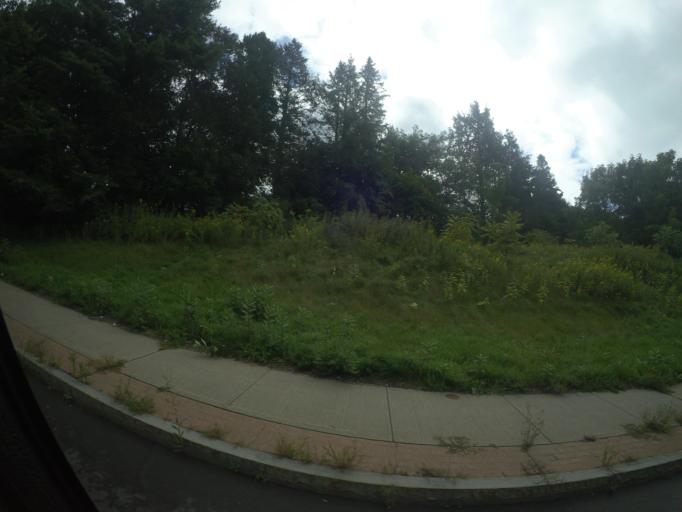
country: US
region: New York
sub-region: Albany County
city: Green Island
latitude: 42.7410
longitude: -73.6549
